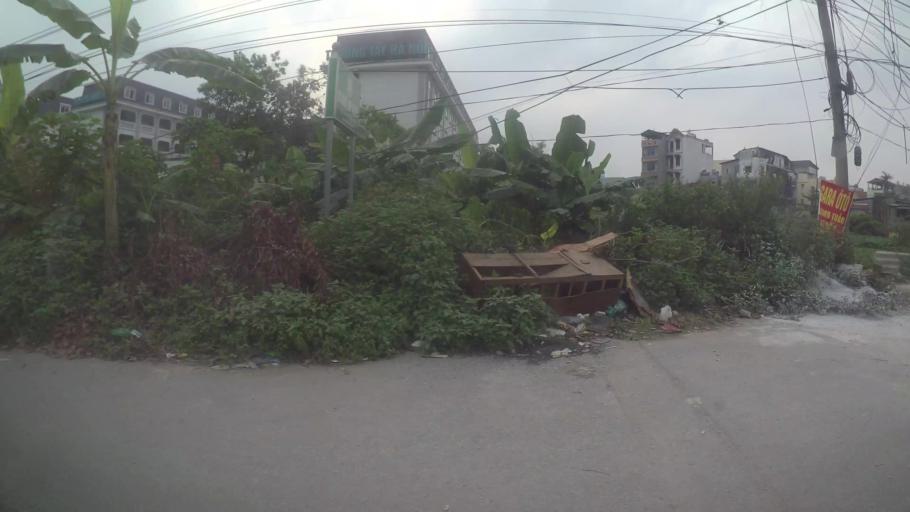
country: VN
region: Ha Noi
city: Cau Dien
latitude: 21.0420
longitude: 105.7517
